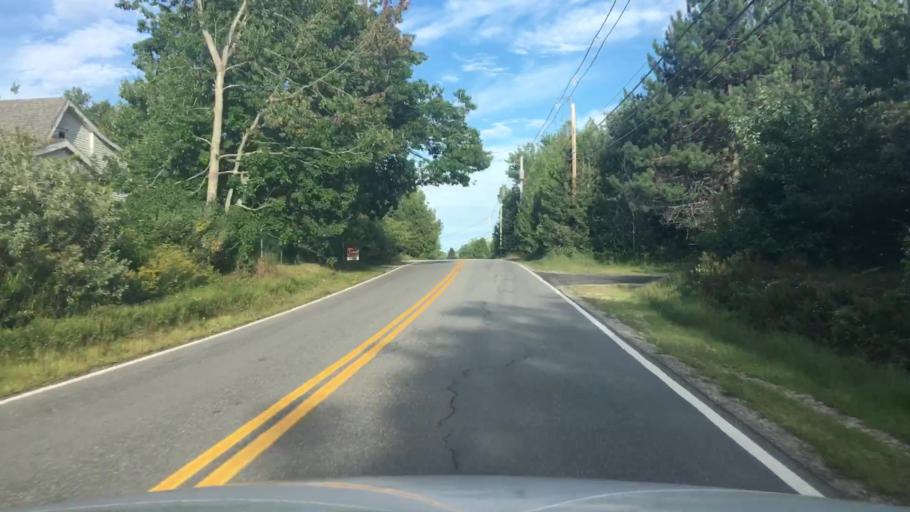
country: US
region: Maine
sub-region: Hancock County
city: Trenton
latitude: 44.4374
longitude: -68.3816
